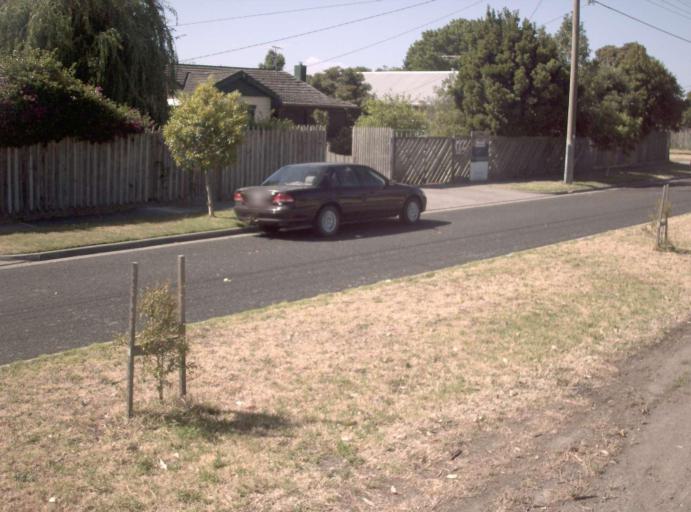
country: AU
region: Victoria
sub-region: Frankston
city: Frankston East
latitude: -38.1255
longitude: 145.1384
